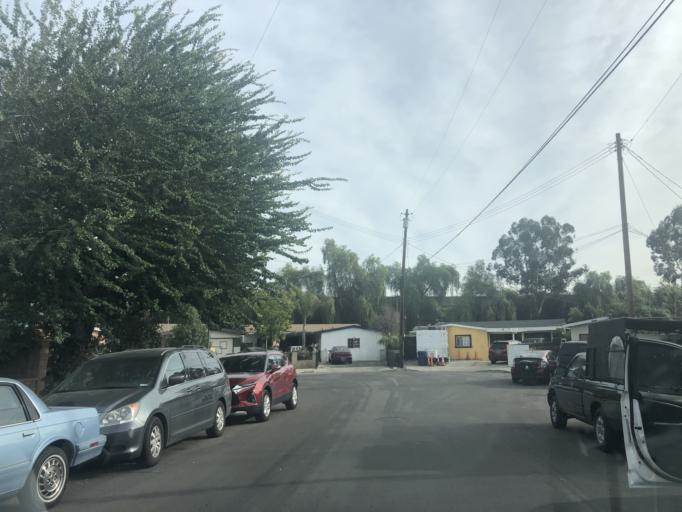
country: US
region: California
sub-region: Los Angeles County
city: San Fernando
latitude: 34.2718
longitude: -118.4320
